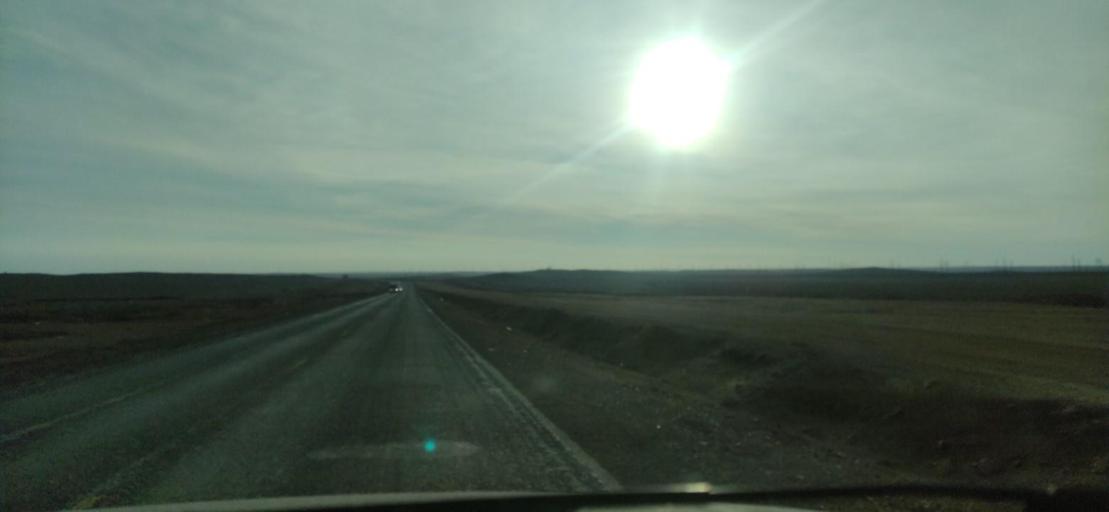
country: KZ
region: Qaraghandy
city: Saryshaghan
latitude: 46.1600
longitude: 73.6119
